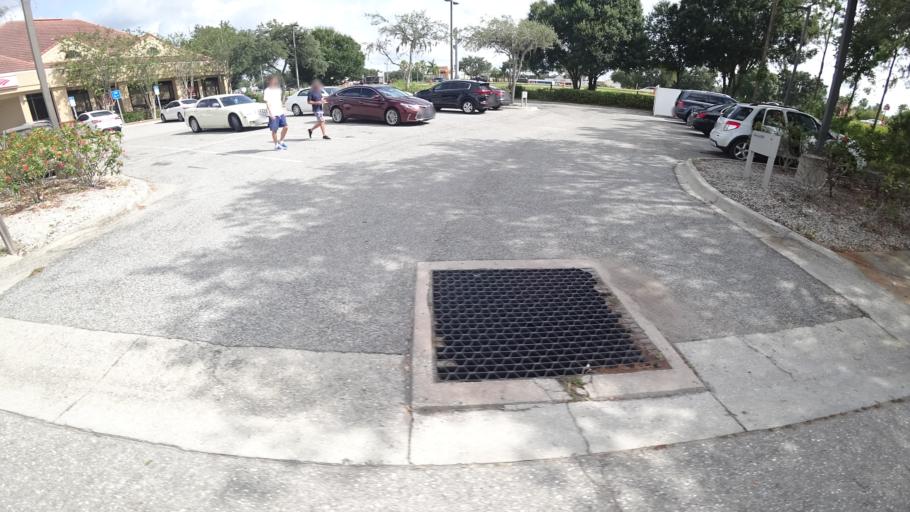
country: US
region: Florida
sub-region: Sarasota County
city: Desoto Lakes
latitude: 27.4425
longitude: -82.4658
